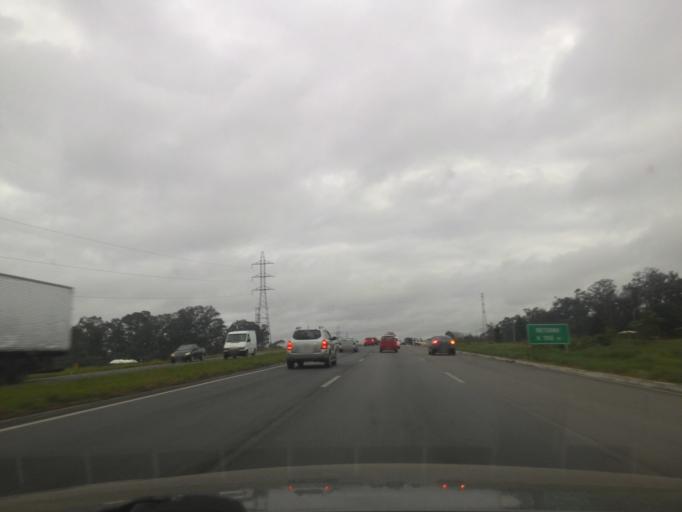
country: BR
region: Parana
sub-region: Araucaria
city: Araucaria
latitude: -25.5494
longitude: -49.3254
